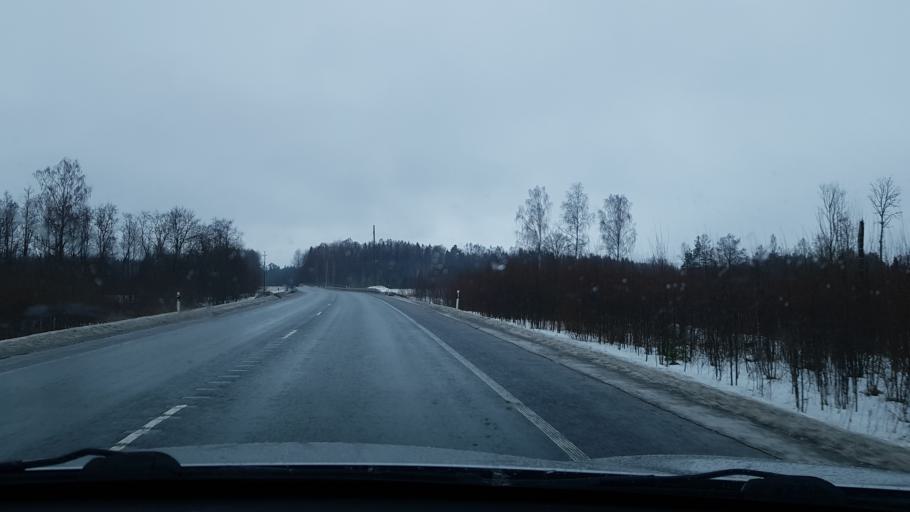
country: EE
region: Raplamaa
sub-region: Kohila vald
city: Kohila
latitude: 59.1361
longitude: 24.7920
